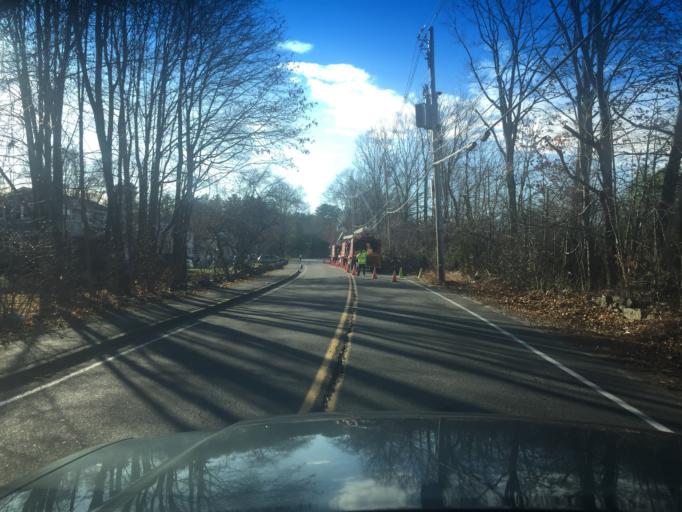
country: US
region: Massachusetts
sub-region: Middlesex County
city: Holliston
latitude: 42.2047
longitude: -71.4489
